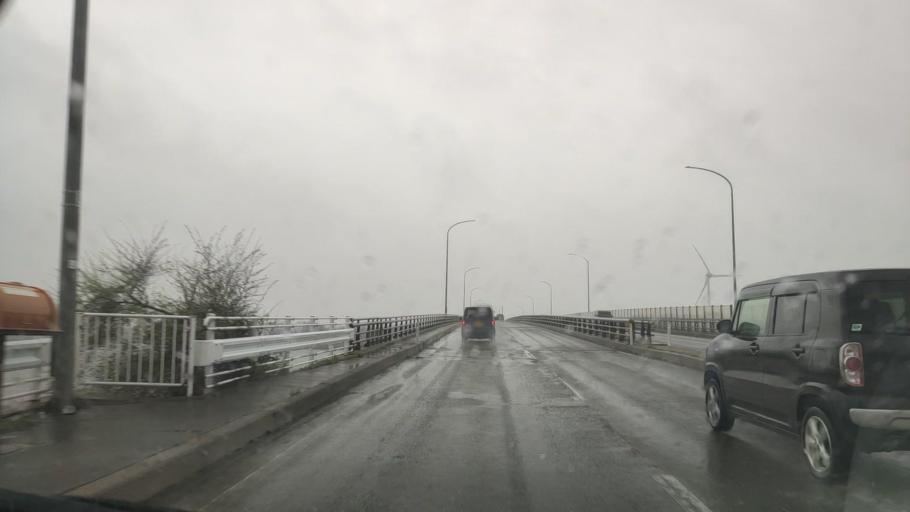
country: JP
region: Akita
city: Tenno
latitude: 39.8970
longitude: 139.9494
